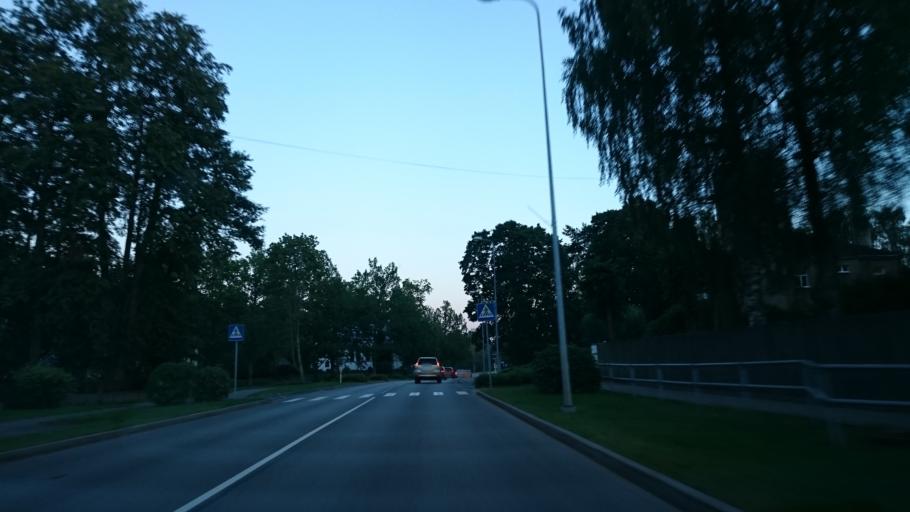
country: LV
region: Saulkrastu
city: Saulkrasti
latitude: 57.2625
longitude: 24.4154
